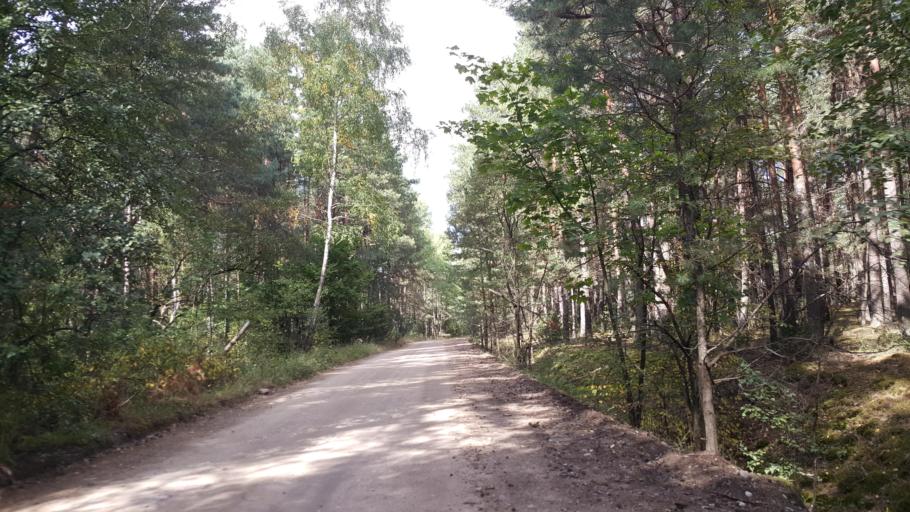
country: BY
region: Brest
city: Kamyanyets
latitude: 52.4361
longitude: 23.9417
